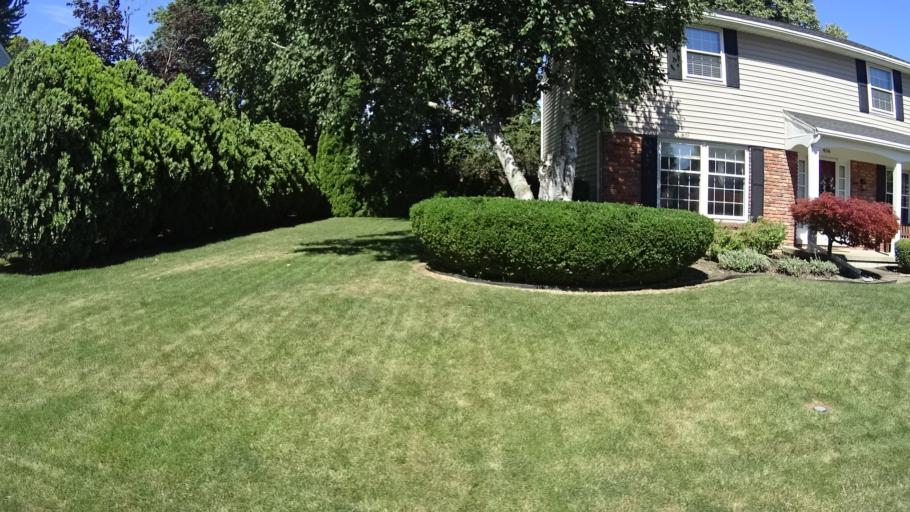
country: US
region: Ohio
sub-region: Erie County
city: Sandusky
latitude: 41.4208
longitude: -82.6950
